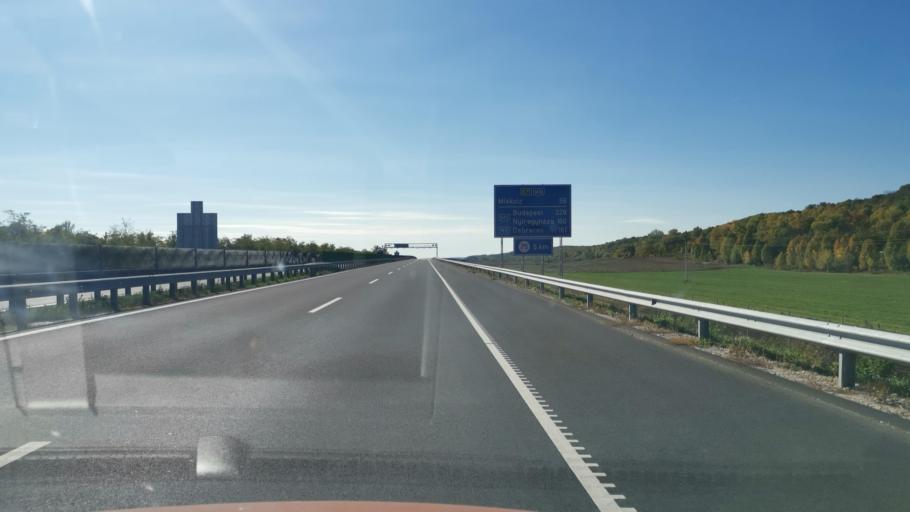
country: HU
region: Borsod-Abauj-Zemplen
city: Gonc
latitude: 48.4636
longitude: 21.1995
